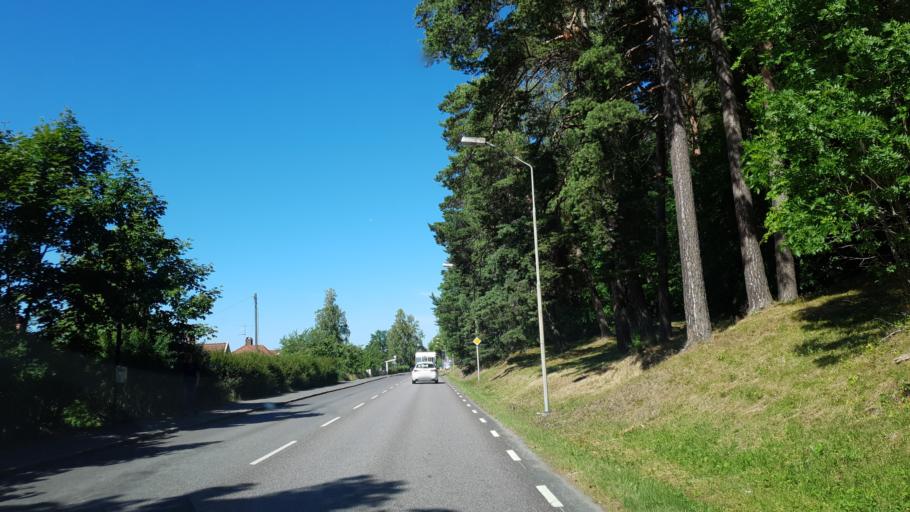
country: SE
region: Joenkoeping
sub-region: Jonkopings Kommun
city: Graenna
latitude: 58.0131
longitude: 14.4583
